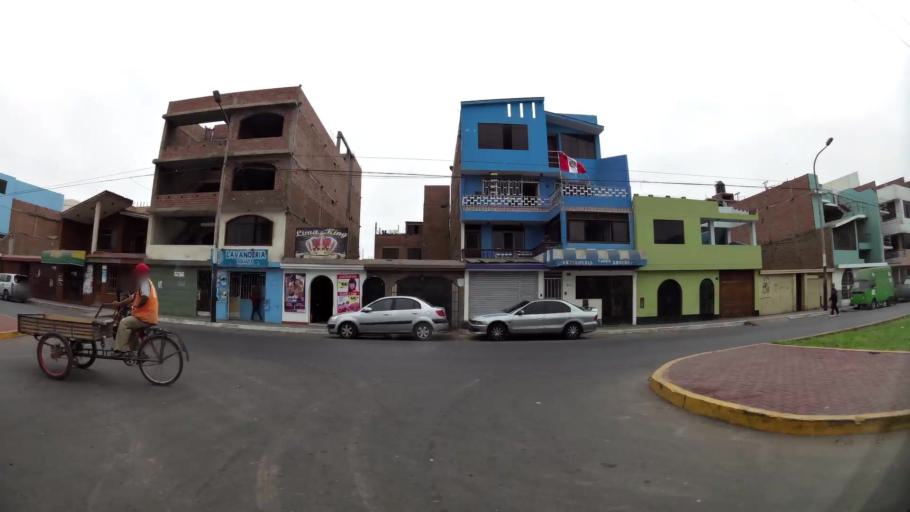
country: PE
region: Callao
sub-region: Callao
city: Callao
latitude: -12.0578
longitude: -77.1053
